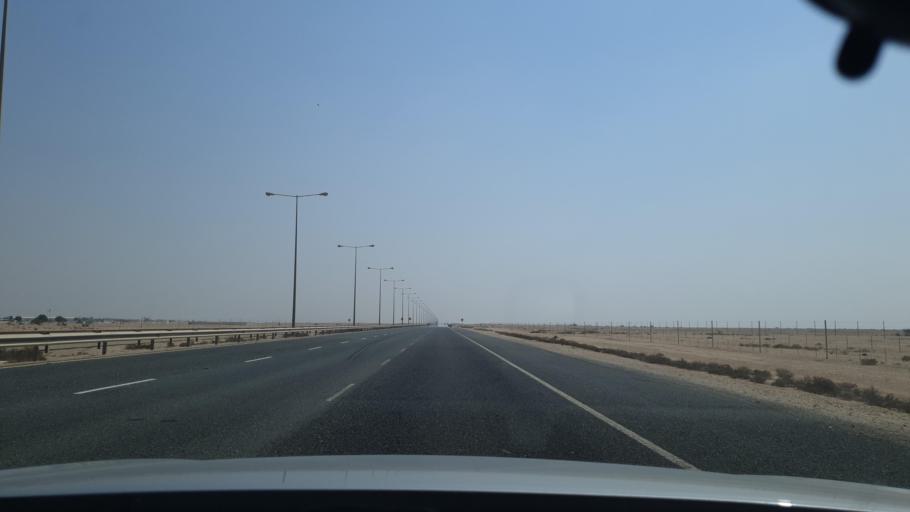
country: QA
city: Al Ghuwayriyah
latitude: 25.8120
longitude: 51.3729
